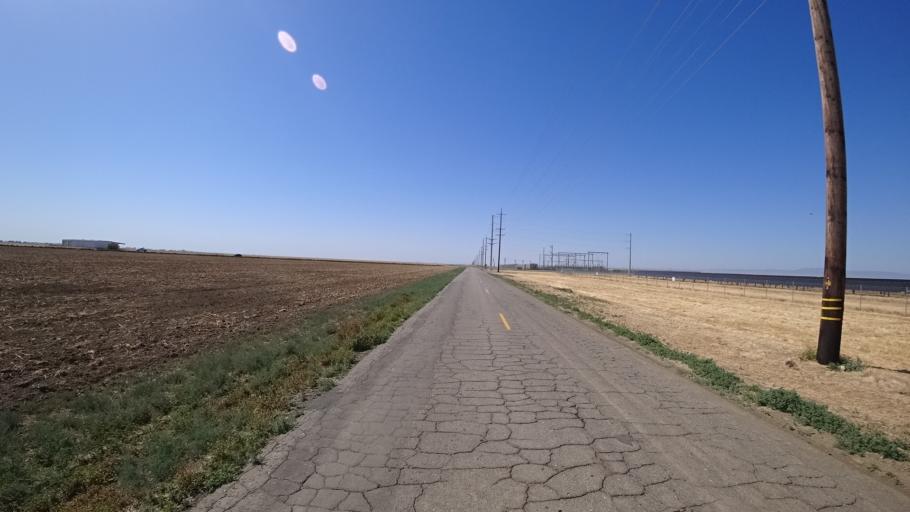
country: US
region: California
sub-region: Kings County
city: Lemoore Station
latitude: 36.2237
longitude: -119.9053
